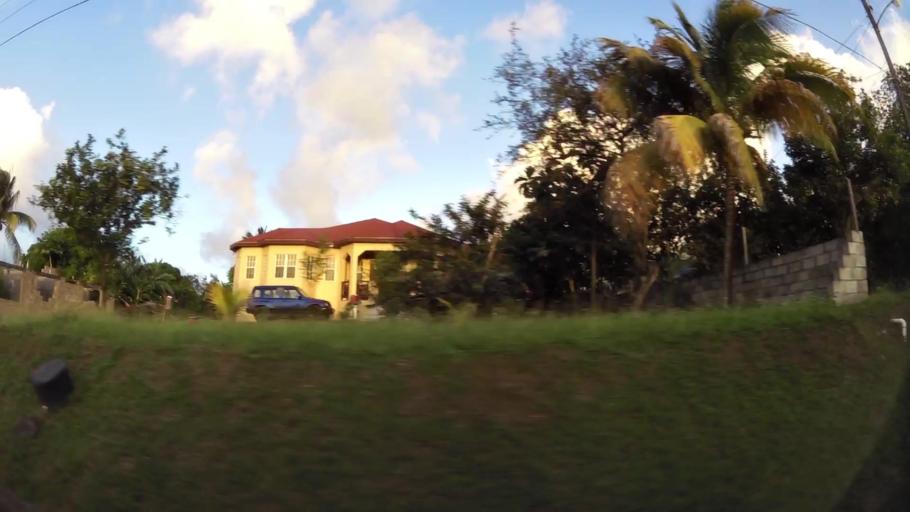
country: KN
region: Saint Anne Sandy Point
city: Sandy Point Town
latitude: 17.3847
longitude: -62.8529
